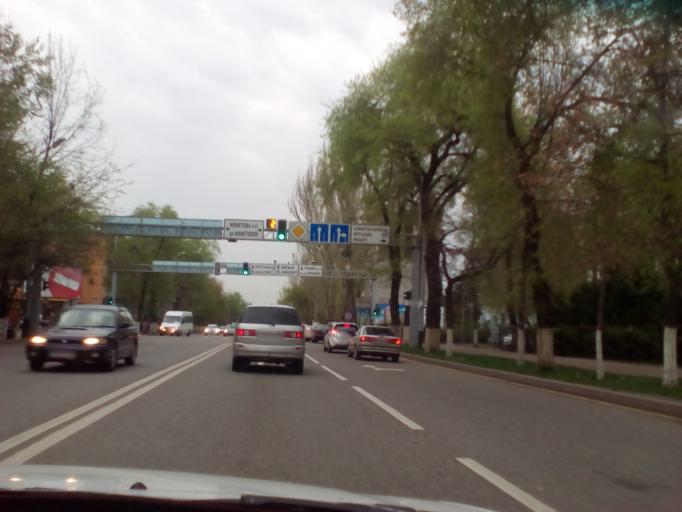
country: KZ
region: Almaty Qalasy
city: Almaty
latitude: 43.2667
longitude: 76.9453
